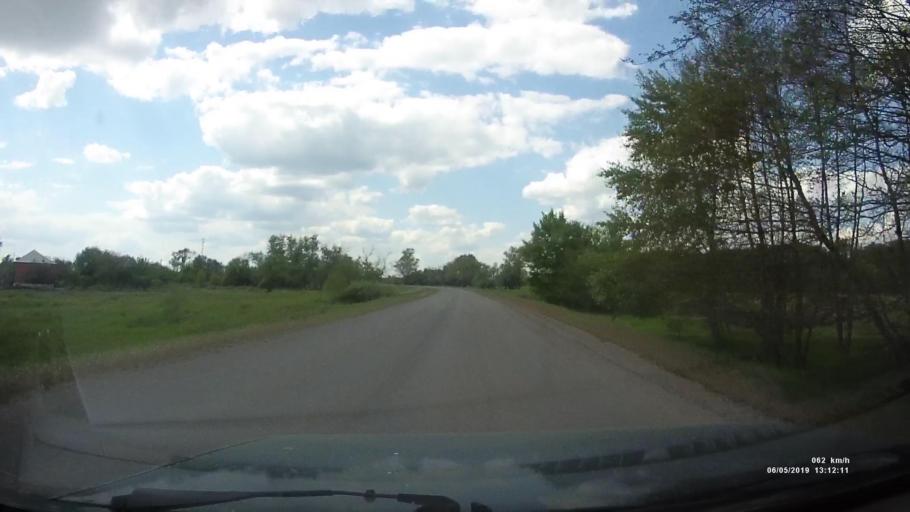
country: RU
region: Rostov
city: Ust'-Donetskiy
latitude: 47.7550
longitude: 40.9503
